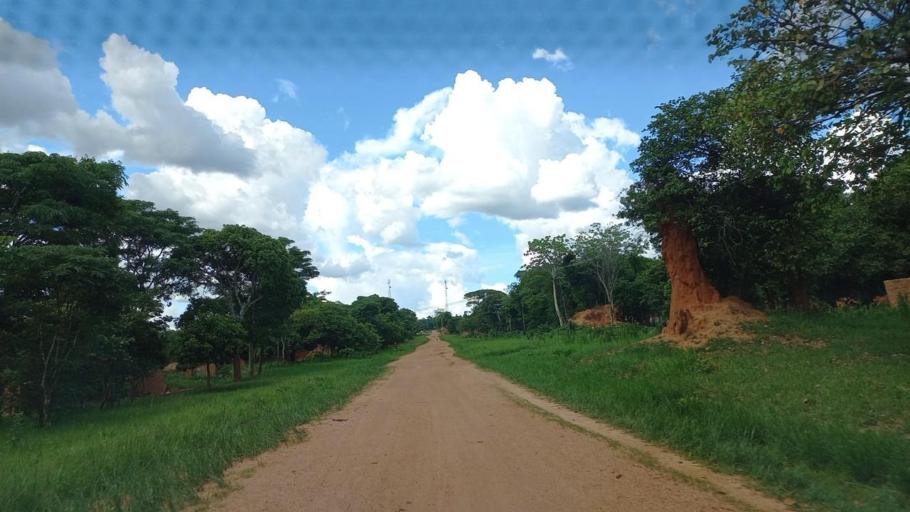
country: ZM
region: North-Western
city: Mwinilunga
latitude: -12.0749
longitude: 24.3009
